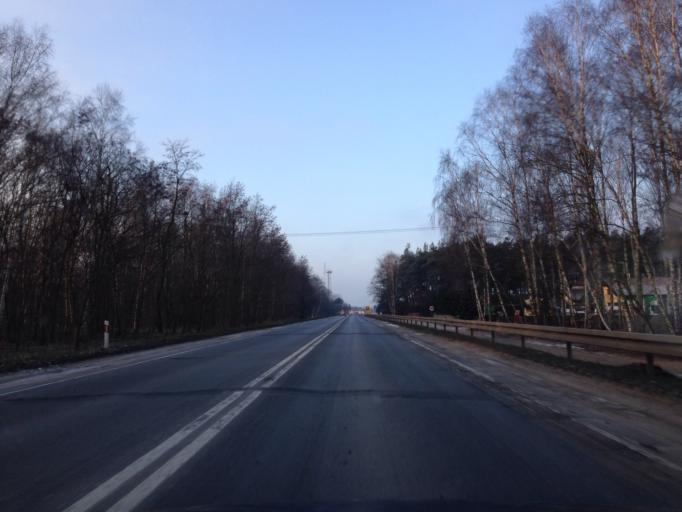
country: PL
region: Greater Poland Voivodeship
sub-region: Powiat poznanski
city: Kostrzyn
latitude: 52.4689
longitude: 17.1829
